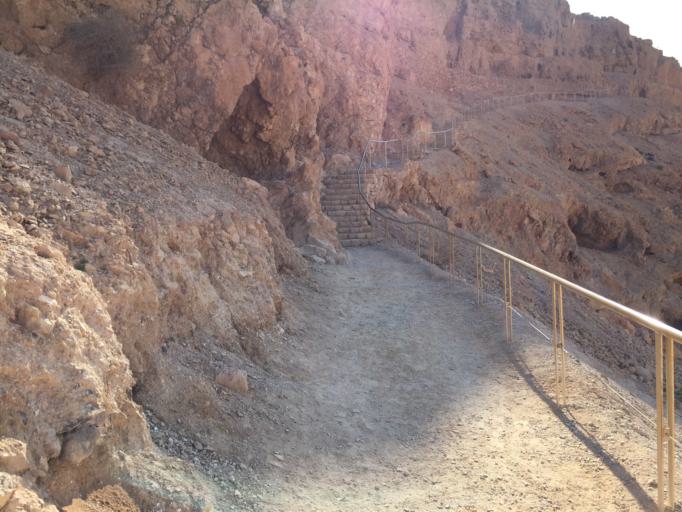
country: IL
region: Southern District
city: `En Boqeq
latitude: 31.3163
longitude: 35.3523
